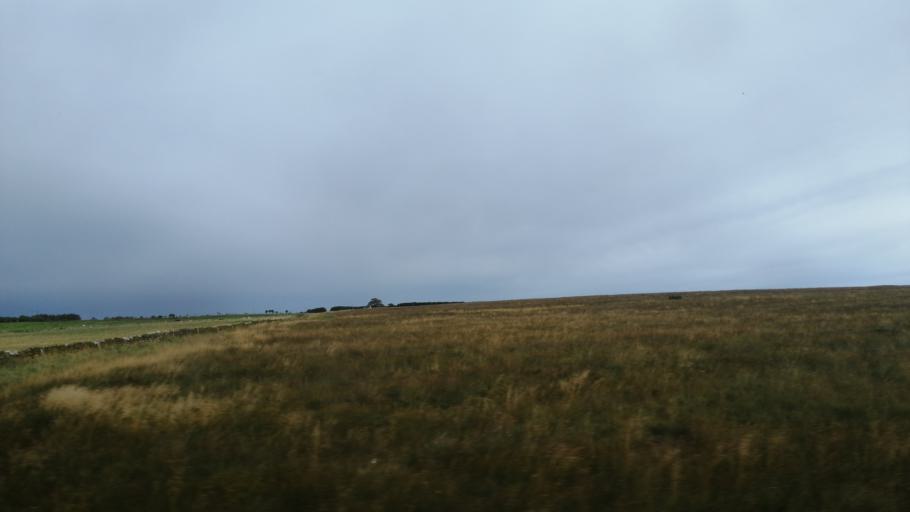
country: GB
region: Scotland
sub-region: Highland
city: Thurso
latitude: 58.4924
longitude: -3.5307
